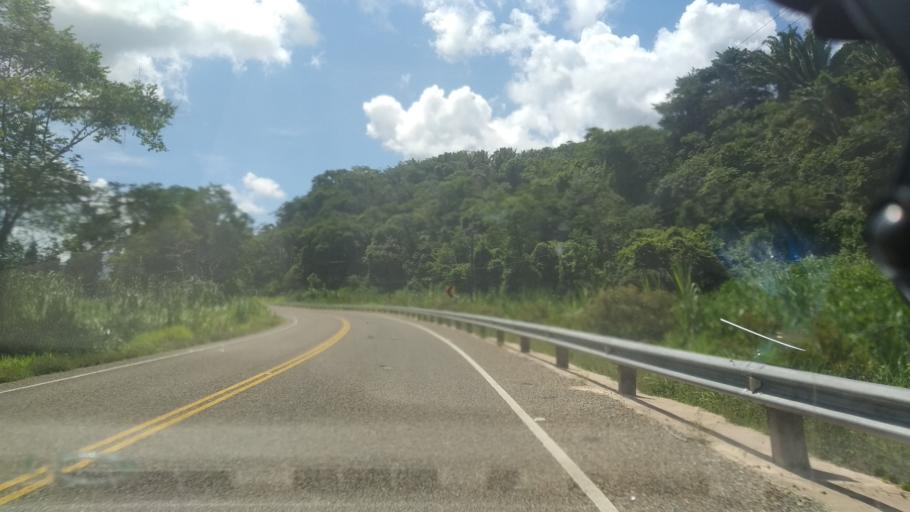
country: BZ
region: Stann Creek
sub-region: Dangriga
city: Dangriga
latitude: 17.0065
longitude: -88.4622
